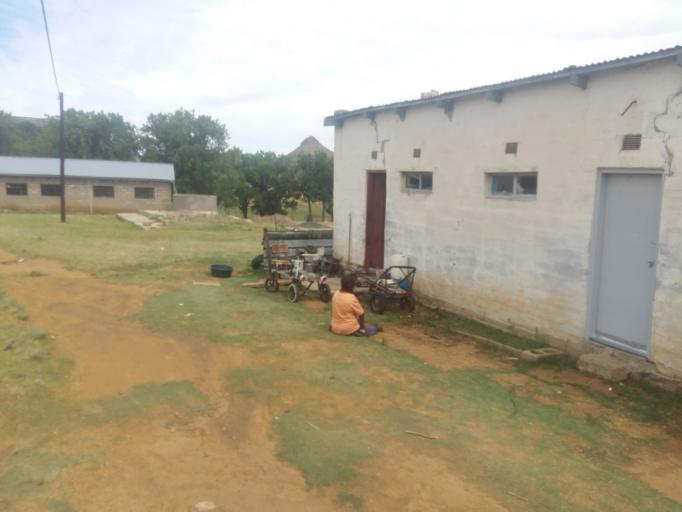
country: LS
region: Mafeteng
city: Mafeteng
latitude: -29.6991
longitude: 27.4310
